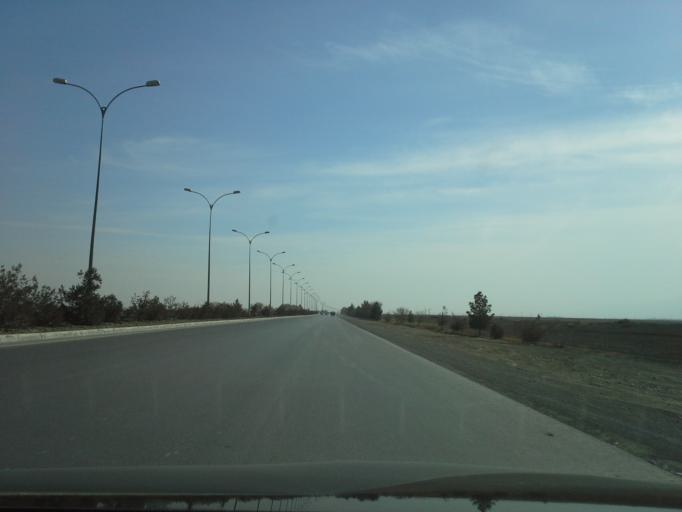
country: TM
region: Ahal
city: Abadan
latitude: 38.1278
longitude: 58.0284
